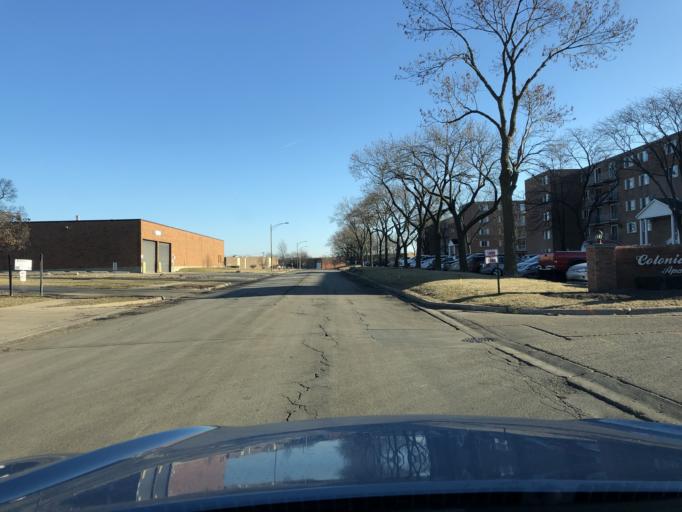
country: US
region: Illinois
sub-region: DuPage County
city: Roselle
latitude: 41.9870
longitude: -88.0438
